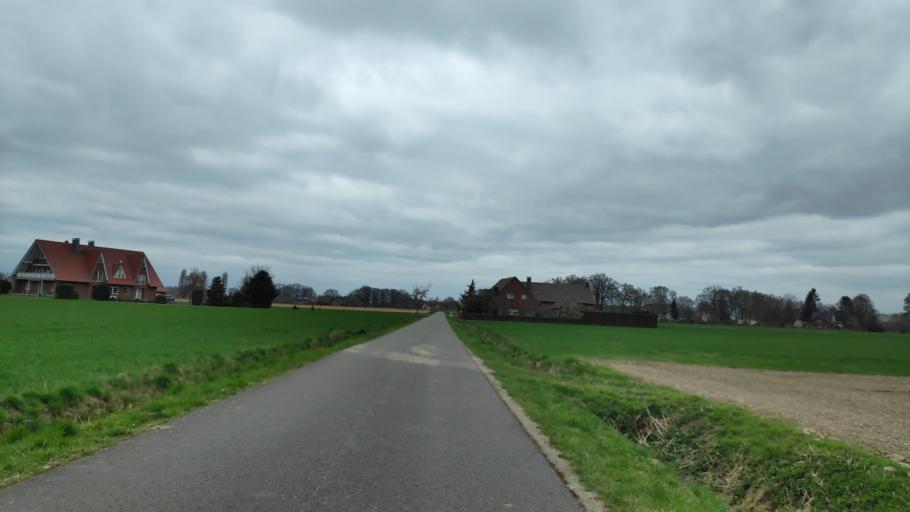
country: DE
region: North Rhine-Westphalia
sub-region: Regierungsbezirk Detmold
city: Minden
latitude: 52.3263
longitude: 8.8565
